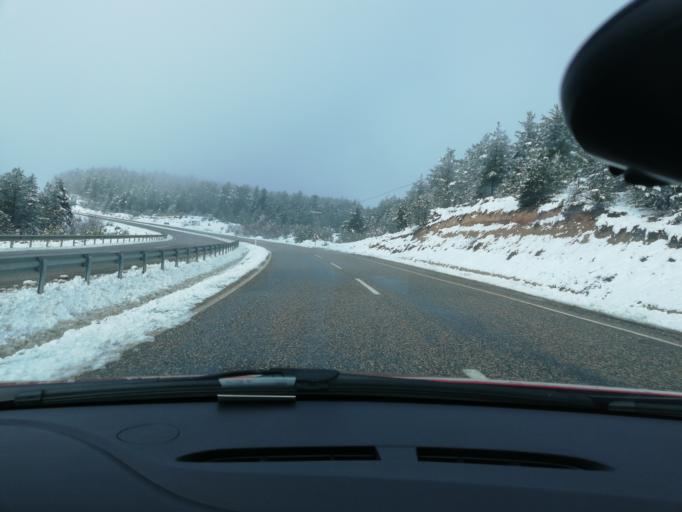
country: TR
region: Kastamonu
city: Akkaya
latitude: 41.3003
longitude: 33.5340
